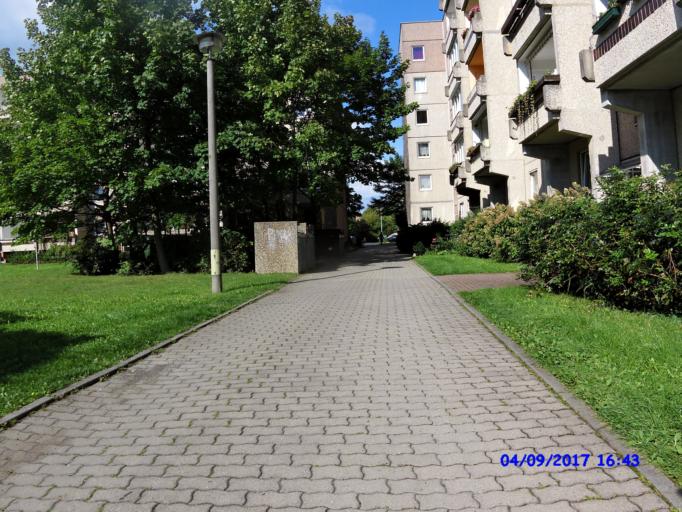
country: DE
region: Saxony
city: Taucha
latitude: 51.3569
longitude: 12.4578
